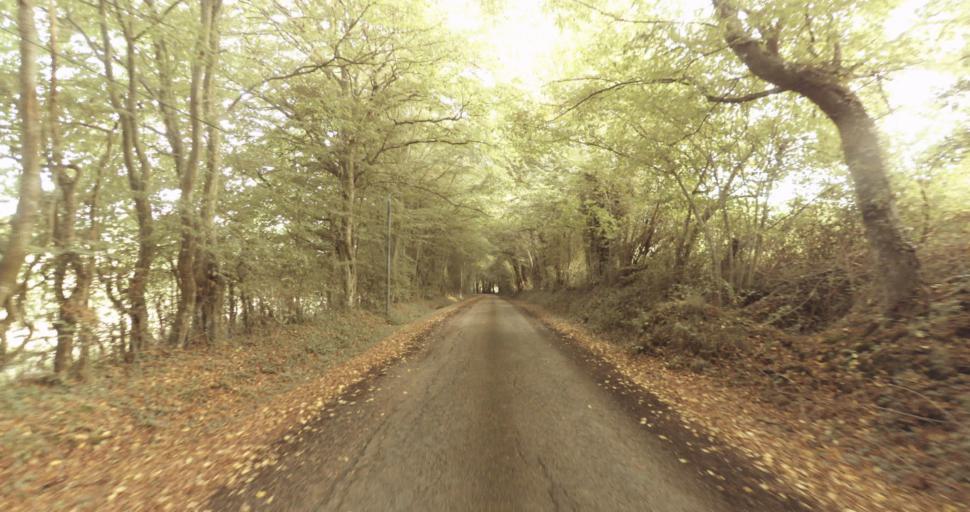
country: FR
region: Lower Normandy
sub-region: Departement de l'Orne
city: Vimoutiers
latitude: 48.8979
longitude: 0.2199
